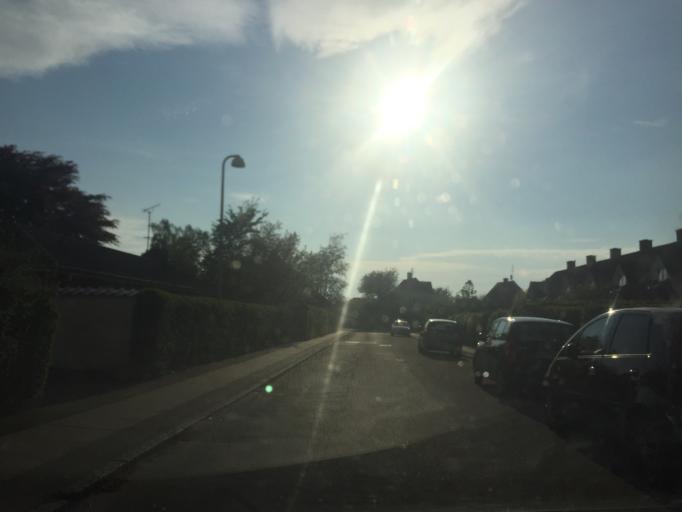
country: DK
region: Capital Region
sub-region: Hoje-Taastrup Kommune
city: Taastrup
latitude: 55.6462
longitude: 12.3054
